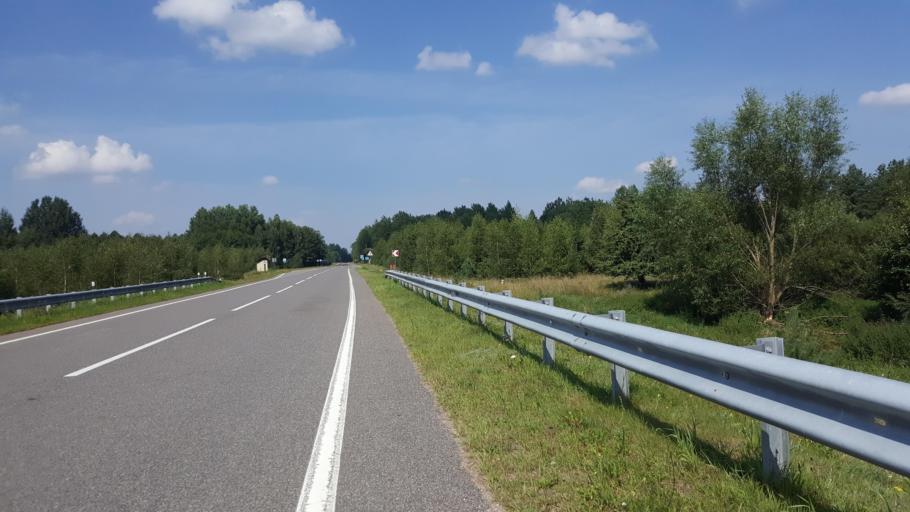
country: BY
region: Brest
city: Kamyanyuki
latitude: 52.5495
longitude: 23.6491
